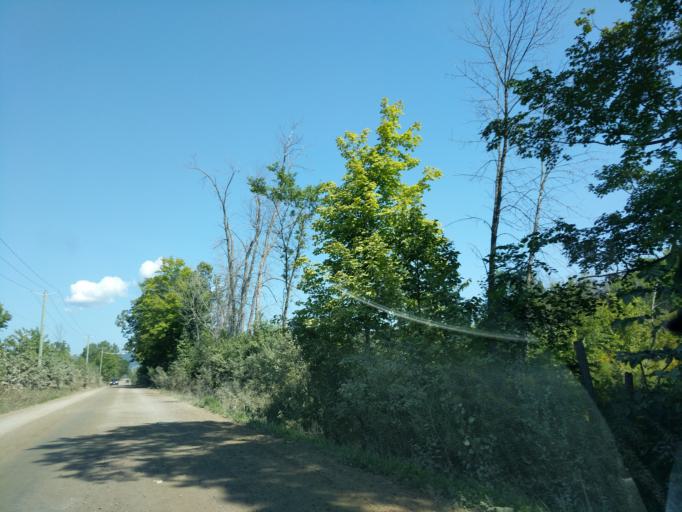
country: CA
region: Ontario
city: Bells Corners
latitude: 45.4445
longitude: -75.9027
